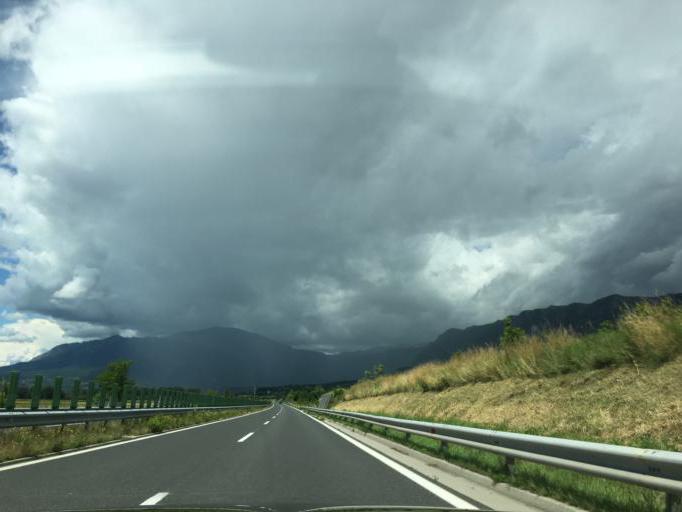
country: SI
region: Vipava
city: Vipava
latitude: 45.8604
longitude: 13.9393
